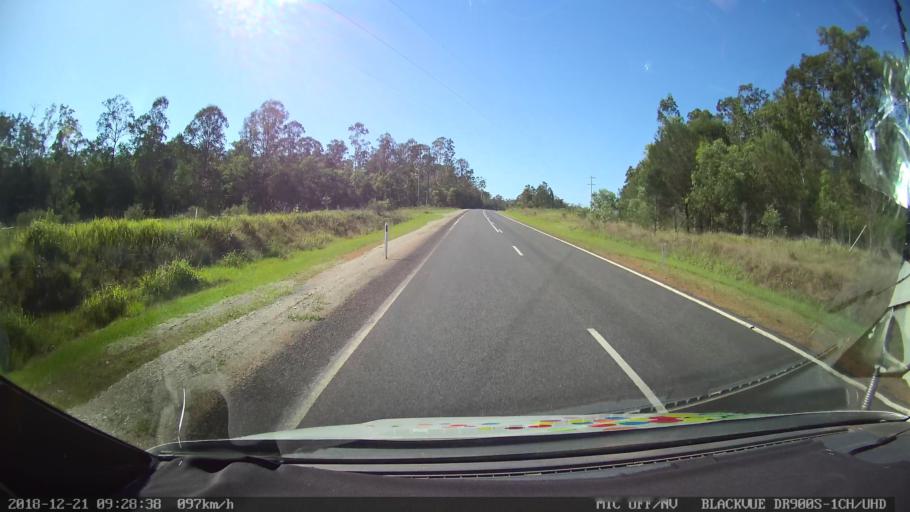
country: AU
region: New South Wales
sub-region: Clarence Valley
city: Maclean
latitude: -29.4202
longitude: 152.9876
